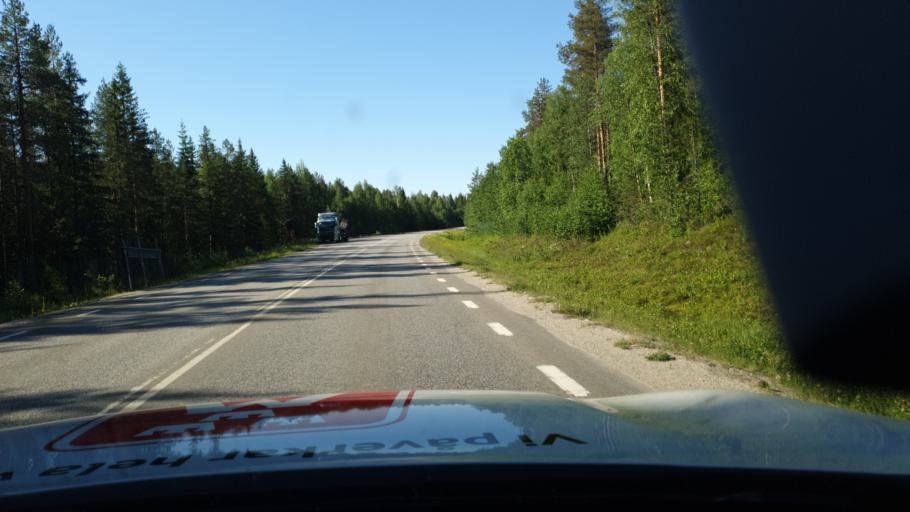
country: SE
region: Vaesterbotten
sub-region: Lycksele Kommun
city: Lycksele
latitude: 64.5810
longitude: 18.6582
